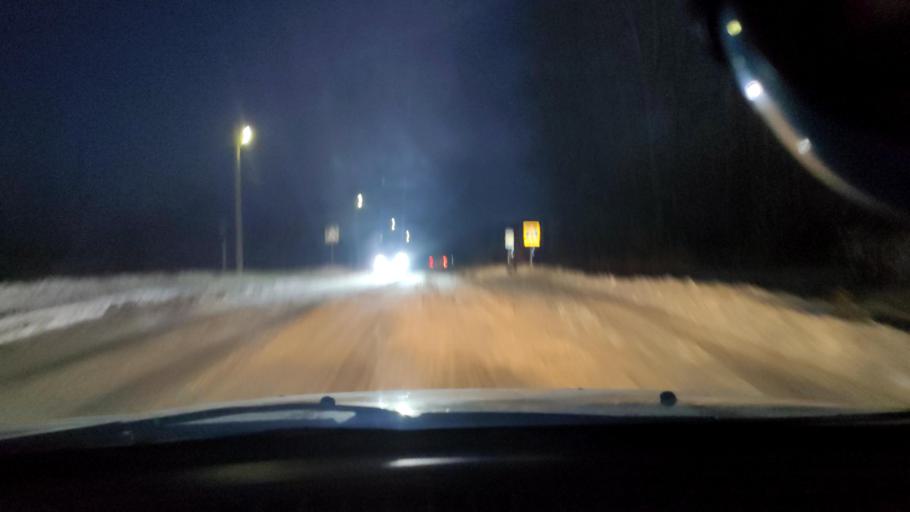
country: RU
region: Perm
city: Kultayevo
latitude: 57.9261
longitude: 55.8848
